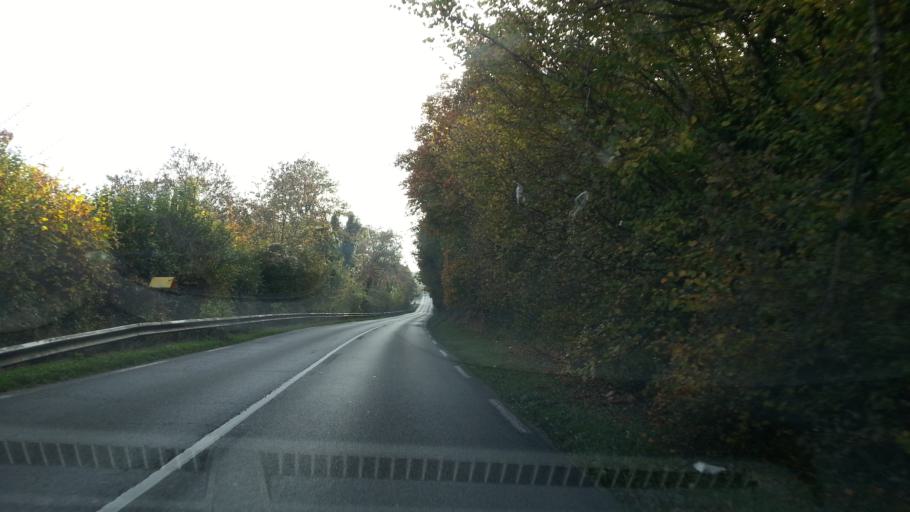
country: FR
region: Picardie
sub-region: Departement de l'Oise
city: Precy-sur-Oise
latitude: 49.1941
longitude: 2.3650
